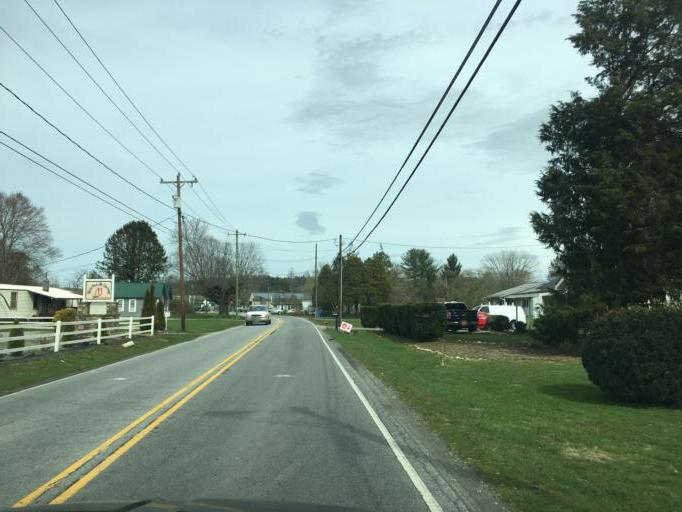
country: US
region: North Carolina
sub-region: Transylvania County
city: Brevard
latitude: 35.2523
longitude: -82.7027
